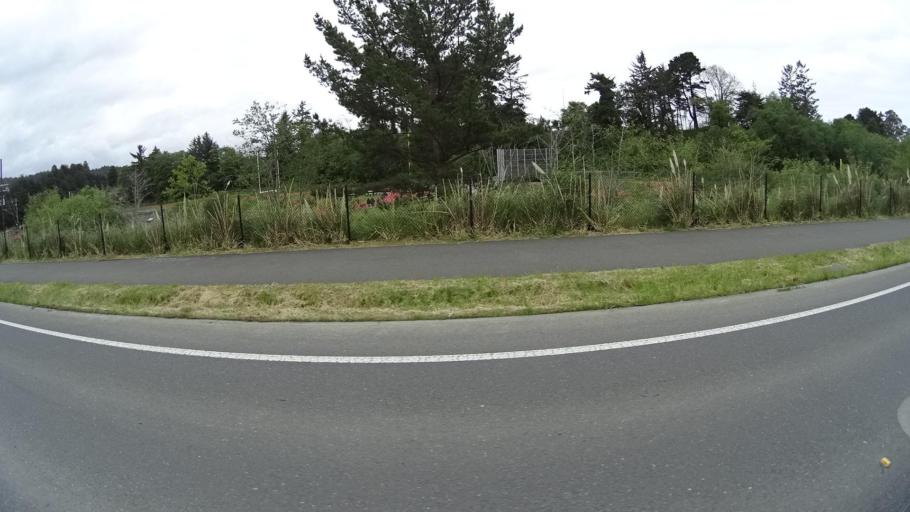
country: US
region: California
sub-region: Humboldt County
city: Arcata
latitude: 40.8795
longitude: -124.0862
